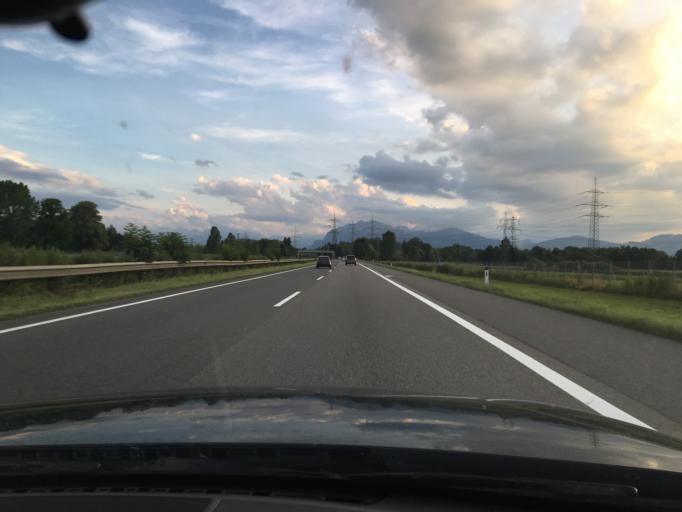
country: AT
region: Vorarlberg
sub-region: Politischer Bezirk Dornbirn
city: Hohenems
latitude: 47.3962
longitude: 9.6890
